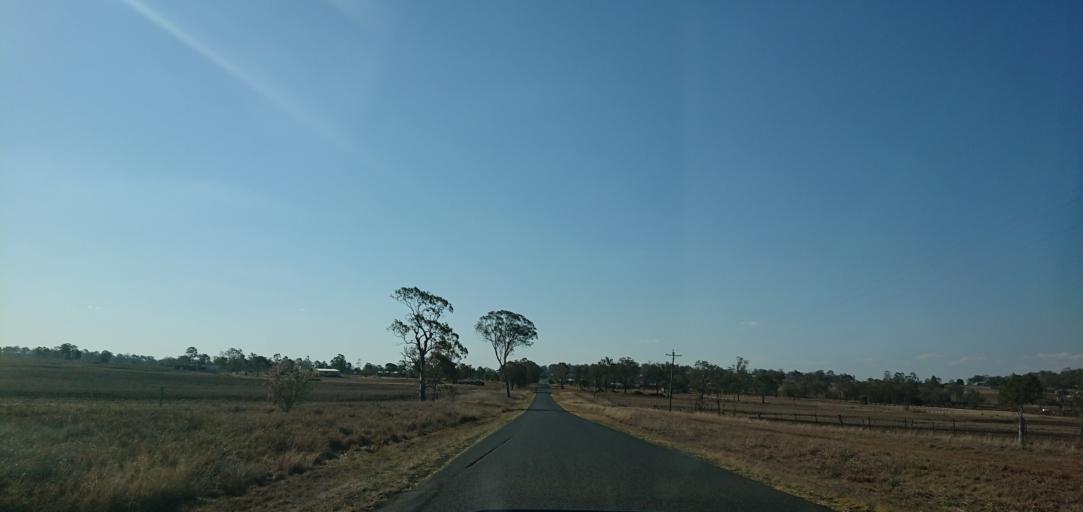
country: AU
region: Queensland
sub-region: Toowoomba
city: Westbrook
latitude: -27.6893
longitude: 151.7146
